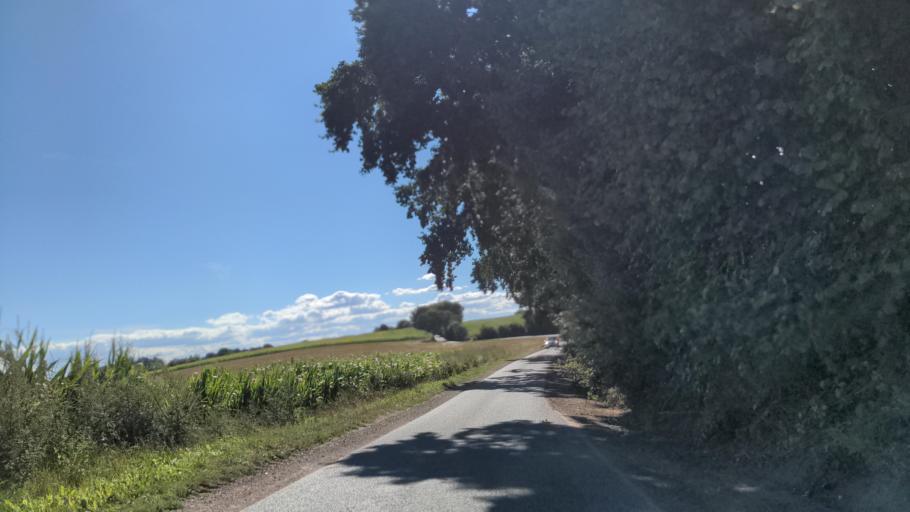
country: DE
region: Schleswig-Holstein
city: Kasseedorf
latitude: 54.1278
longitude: 10.7195
